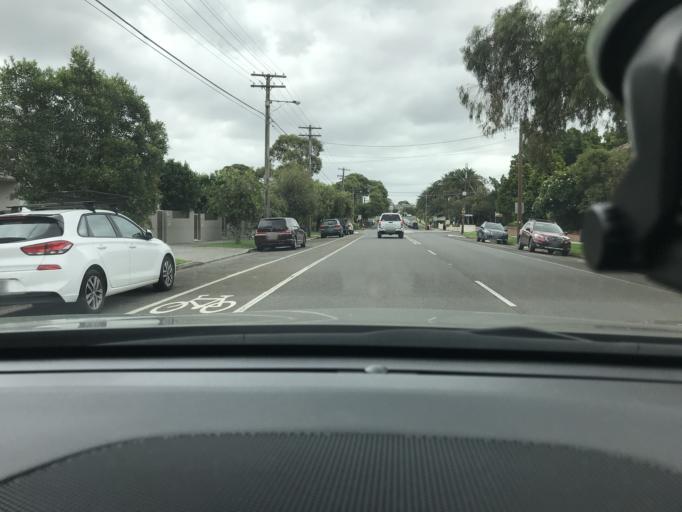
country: AU
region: New South Wales
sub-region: Canada Bay
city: Wareemba
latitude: -33.8521
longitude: 151.1293
